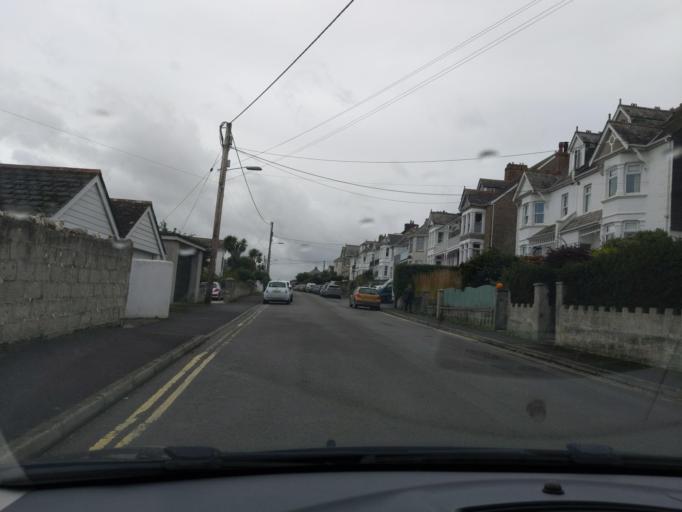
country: GB
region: England
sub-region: Cornwall
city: Padstow
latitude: 50.5386
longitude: -4.9379
